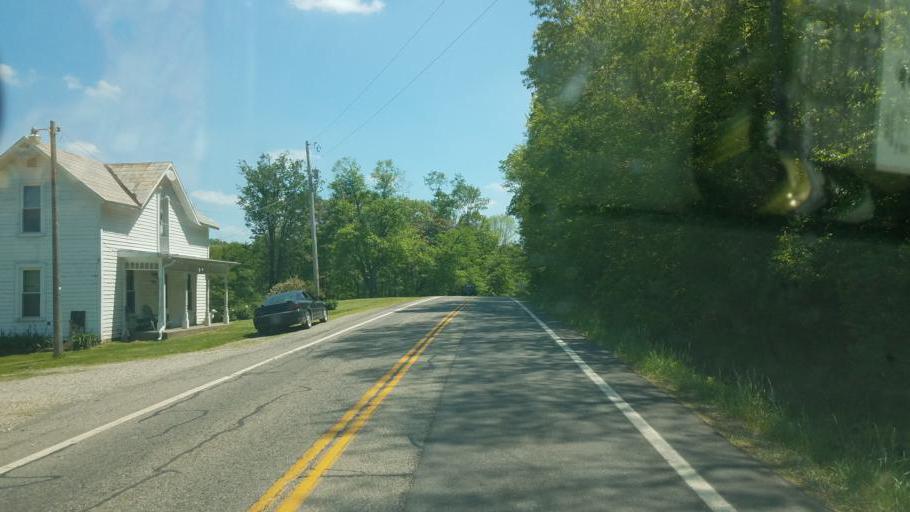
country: US
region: Ohio
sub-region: Muskingum County
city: Frazeysburg
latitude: 40.2013
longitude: -82.2346
